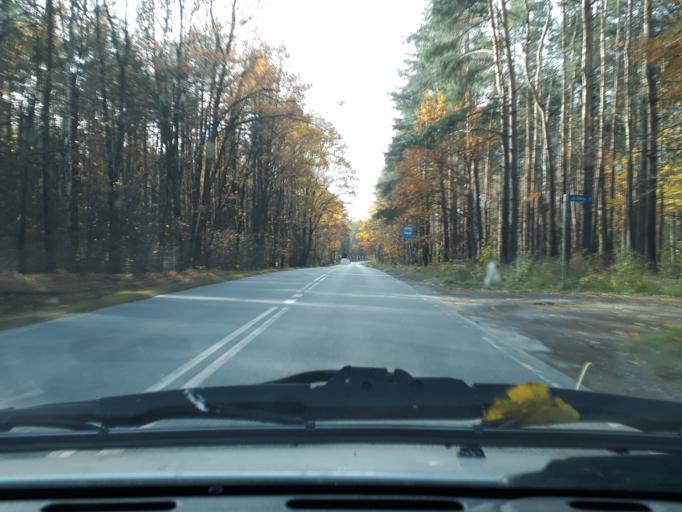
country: PL
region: Silesian Voivodeship
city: Wozniki
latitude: 50.5766
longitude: 19.0292
